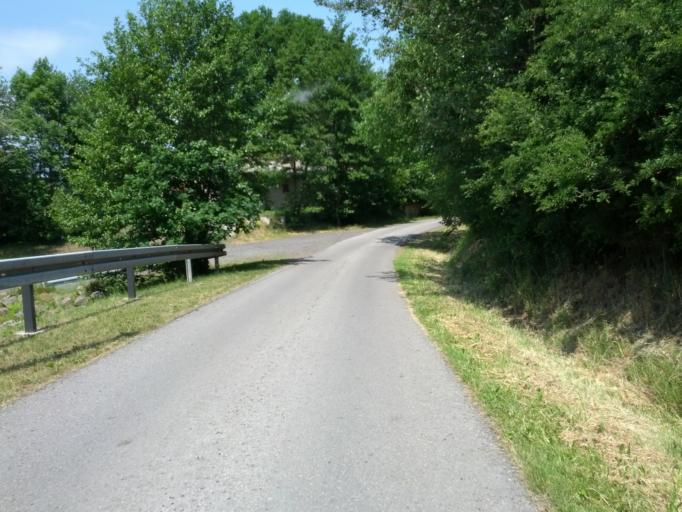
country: DE
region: Thuringia
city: Weilar
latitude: 50.7533
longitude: 10.1585
